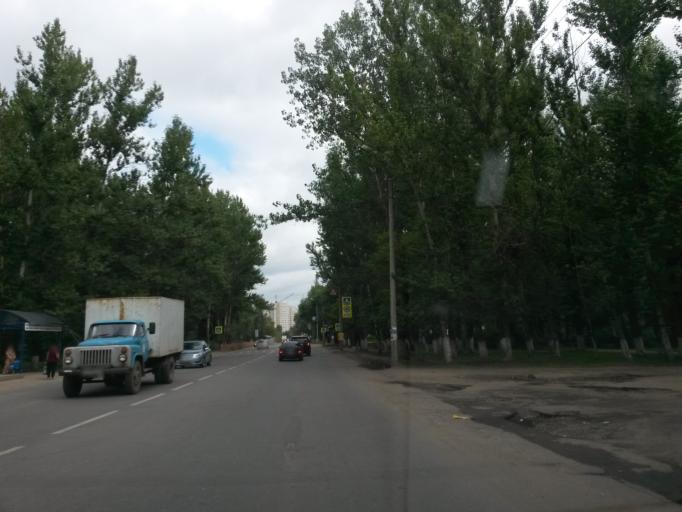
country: RU
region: Jaroslavl
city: Yaroslavl
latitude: 57.5725
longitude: 39.8609
